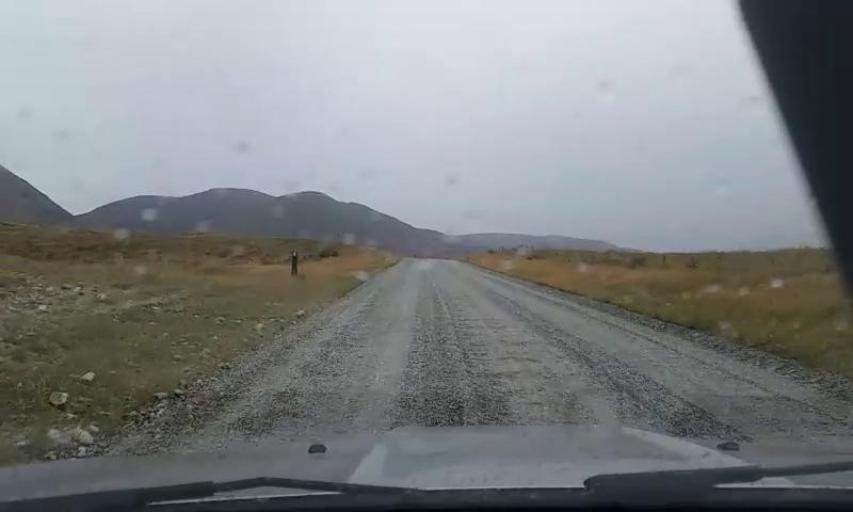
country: NZ
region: Canterbury
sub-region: Ashburton District
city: Methven
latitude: -43.6156
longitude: 171.0982
